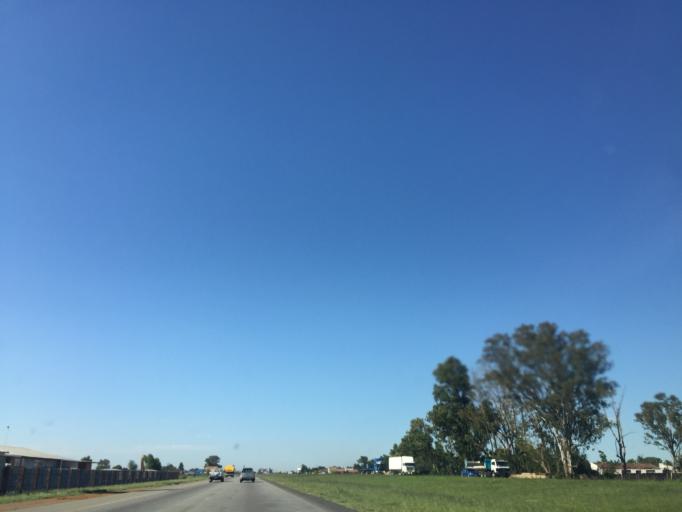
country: ZA
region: Gauteng
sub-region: Sedibeng District Municipality
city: Meyerton
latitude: -26.5506
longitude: 28.0047
